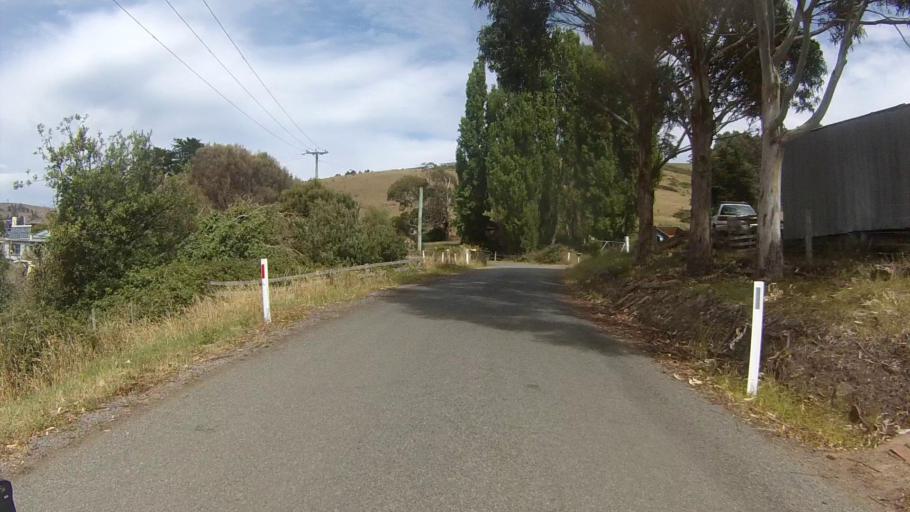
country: AU
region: Tasmania
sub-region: Sorell
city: Sorell
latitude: -42.8076
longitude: 147.8330
